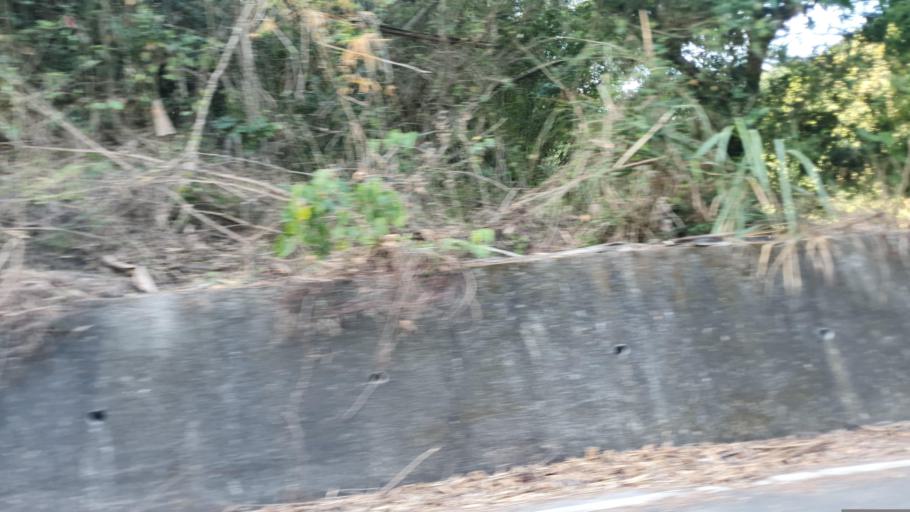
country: TW
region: Taiwan
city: Yujing
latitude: 23.0179
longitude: 120.3973
